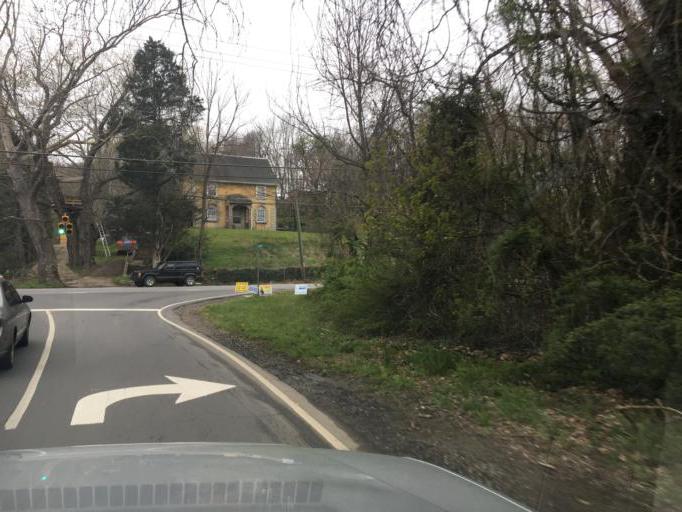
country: US
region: North Carolina
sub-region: Buncombe County
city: Woodfin
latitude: 35.6144
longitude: -82.6283
